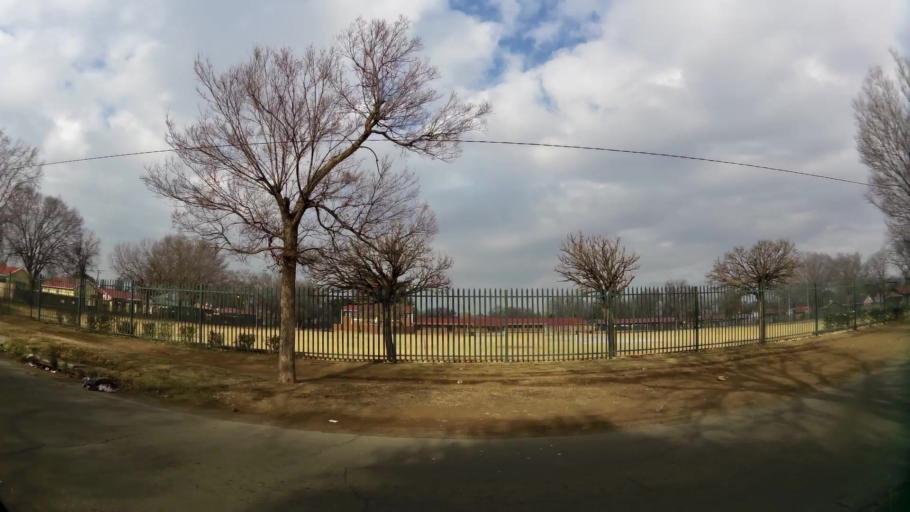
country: ZA
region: Gauteng
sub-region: Sedibeng District Municipality
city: Vanderbijlpark
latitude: -26.7046
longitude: 27.8178
